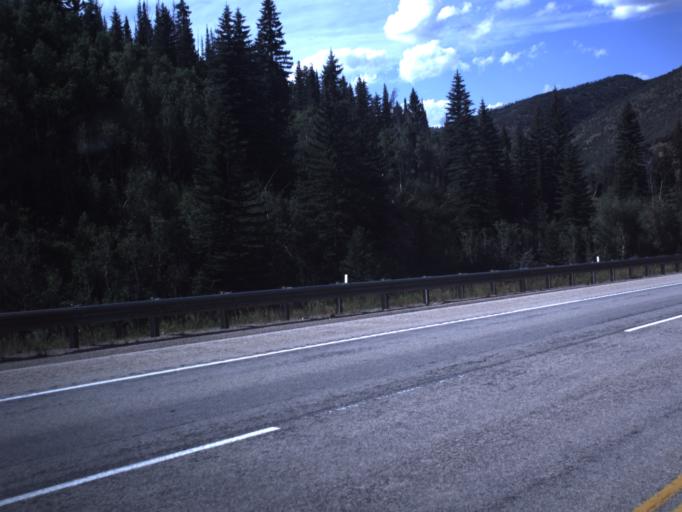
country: US
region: Utah
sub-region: Wasatch County
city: Heber
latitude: 40.3350
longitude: -111.2612
